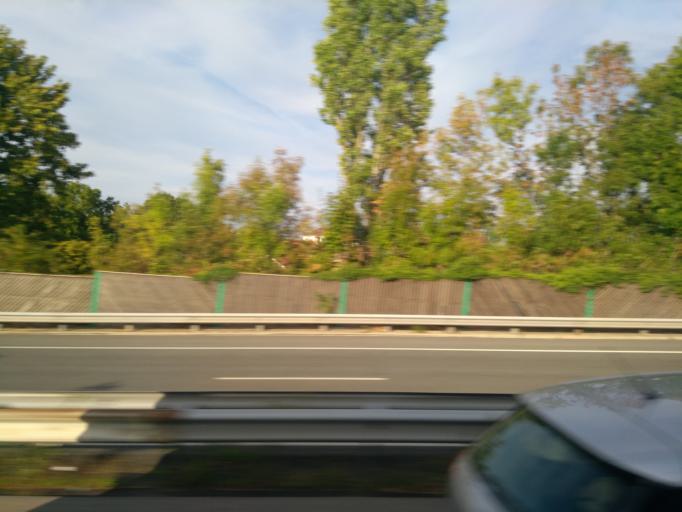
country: FR
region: Rhone-Alpes
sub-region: Departement de l'Isere
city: Saint-Victor-de-Cessieu
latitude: 45.5401
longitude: 5.3900
